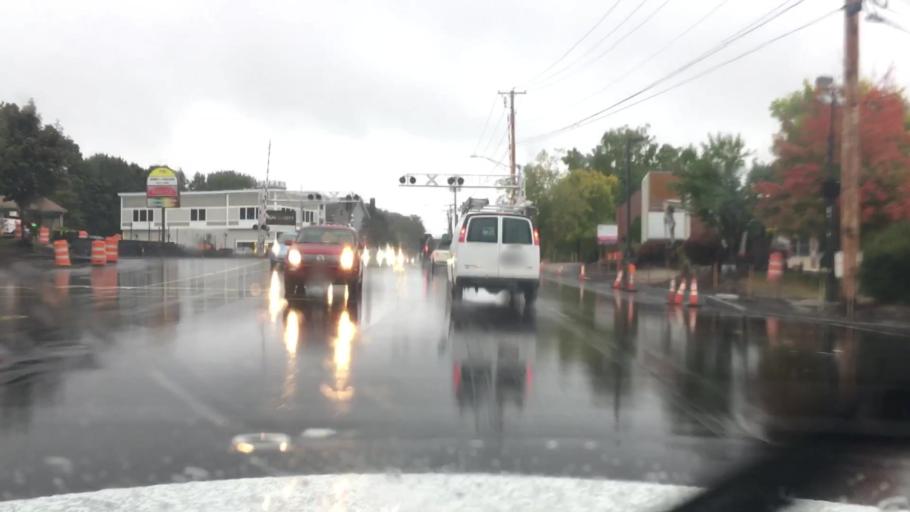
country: US
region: Maine
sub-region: Cumberland County
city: Portland
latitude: 43.6721
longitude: -70.2847
